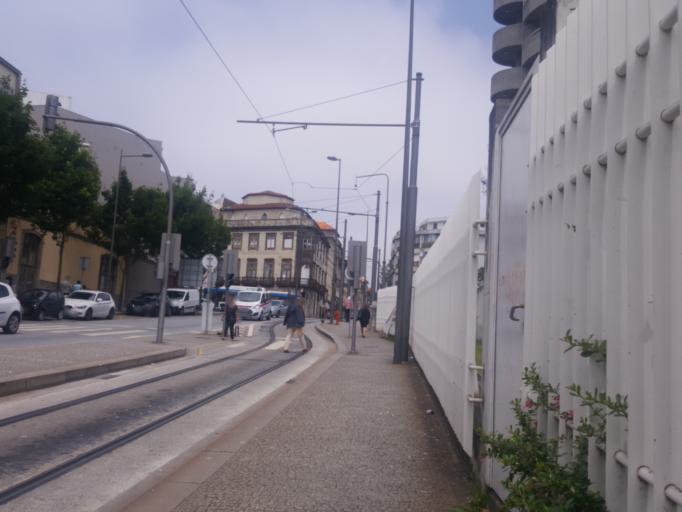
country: PT
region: Porto
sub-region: Porto
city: Porto
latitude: 41.1466
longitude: -8.6202
